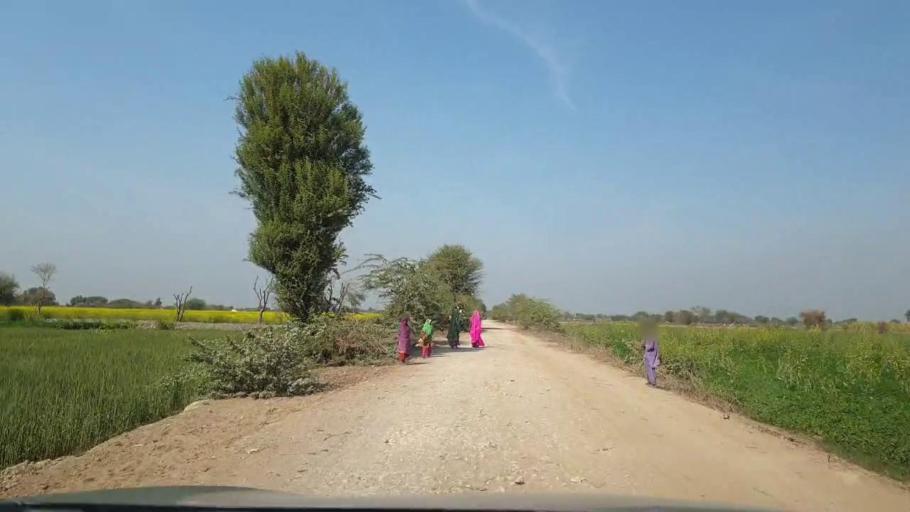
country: PK
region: Sindh
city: Berani
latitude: 25.7031
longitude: 68.7535
